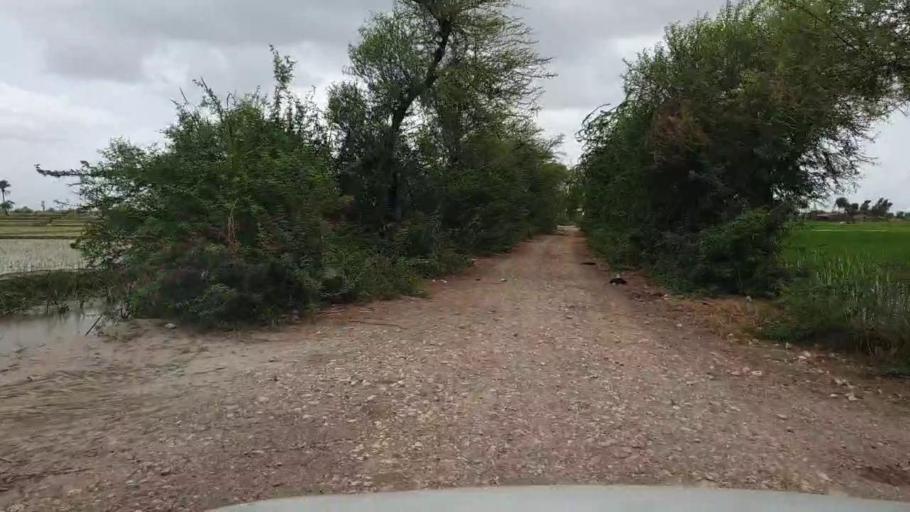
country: PK
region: Sindh
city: Kario
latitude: 24.7481
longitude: 68.4838
